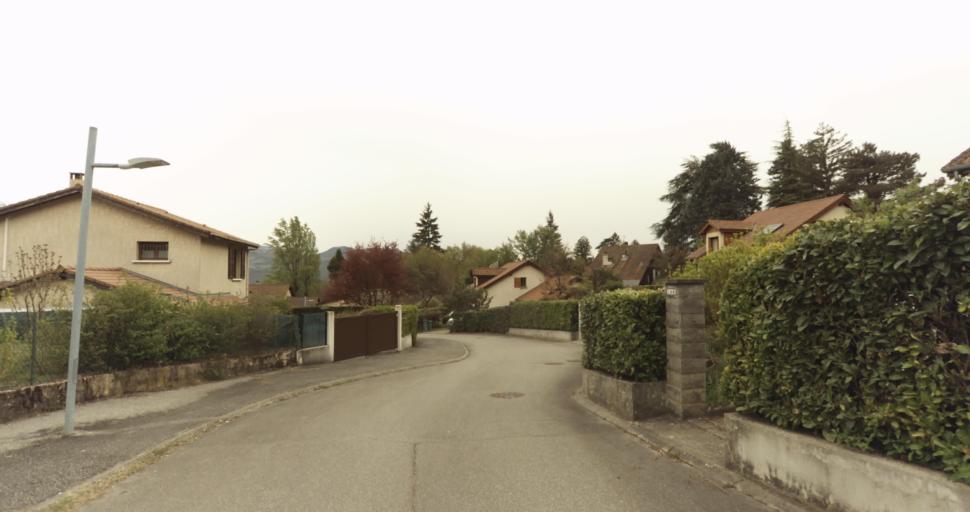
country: FR
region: Rhone-Alpes
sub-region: Departement de l'Isere
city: Biviers
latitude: 45.2326
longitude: 5.8084
